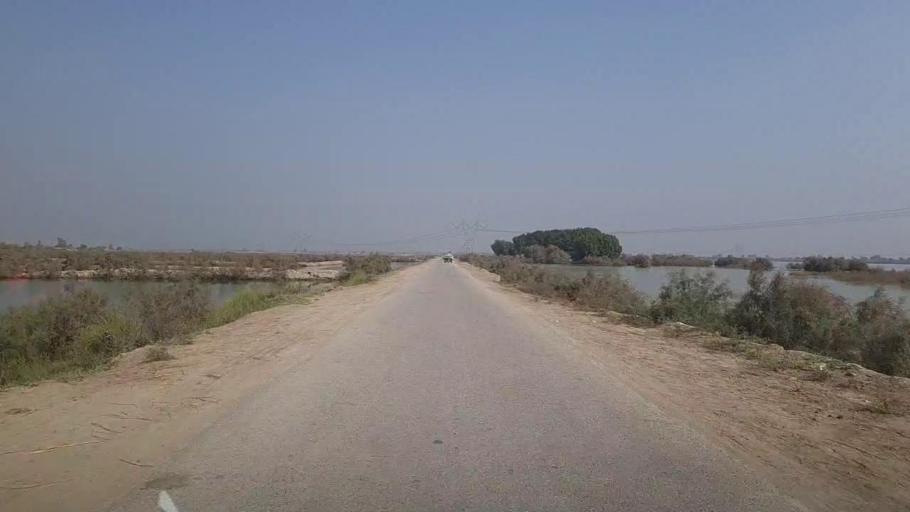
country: PK
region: Sindh
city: Kandhkot
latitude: 28.2252
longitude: 69.1898
